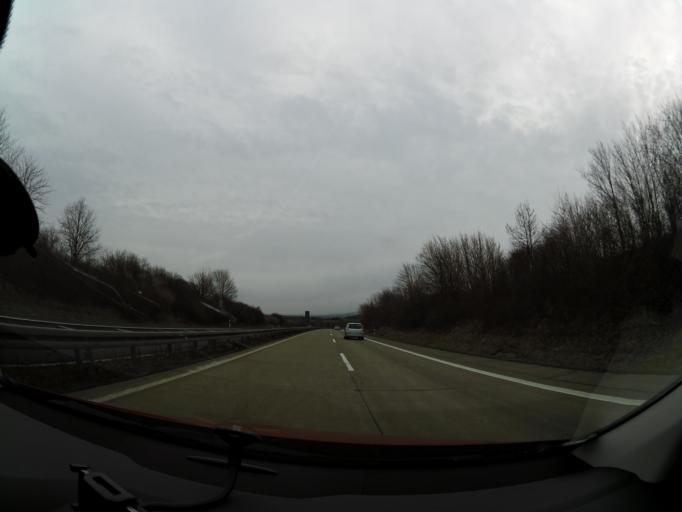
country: DE
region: Lower Saxony
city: Schladen
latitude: 51.9981
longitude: 10.5507
